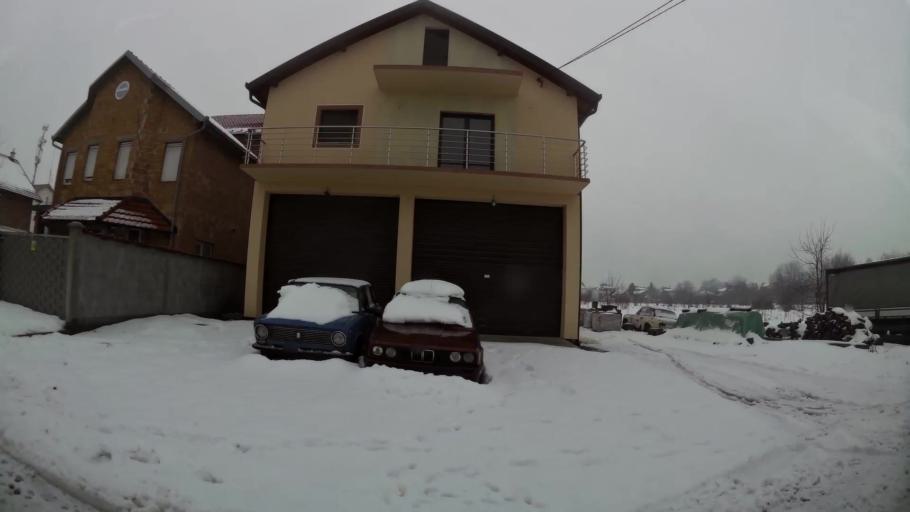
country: RS
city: Novi Banovci
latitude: 44.8777
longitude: 20.3197
